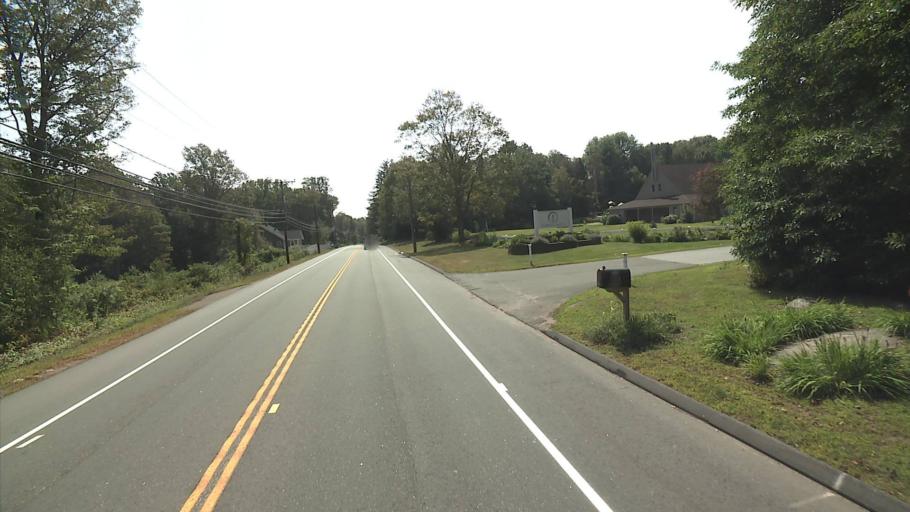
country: US
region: Connecticut
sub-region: New Haven County
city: Guilford
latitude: 41.3528
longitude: -72.6344
